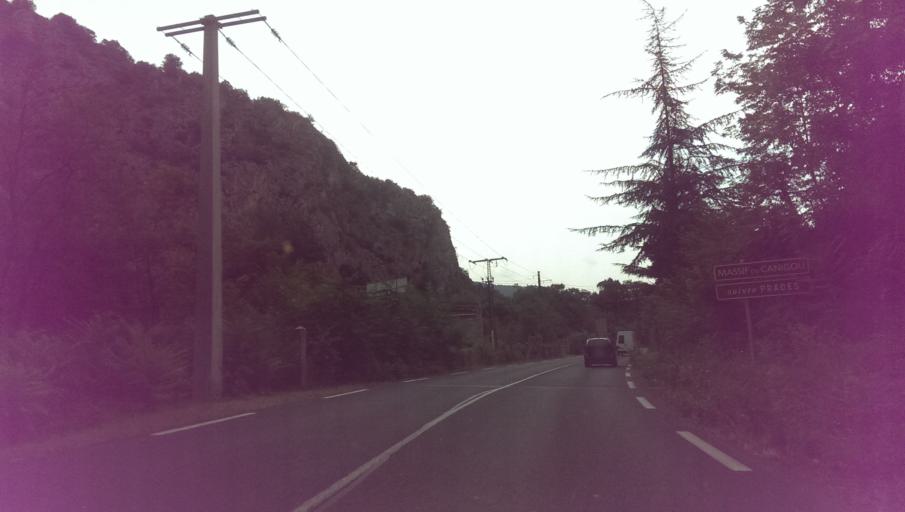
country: FR
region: Languedoc-Roussillon
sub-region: Departement des Pyrenees-Orientales
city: Ria-Sirach
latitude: 42.5948
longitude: 2.3743
